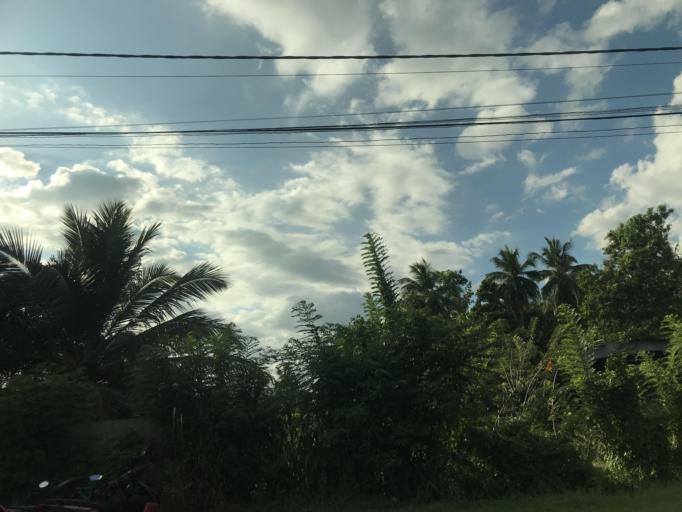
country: LK
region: Western
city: Gampaha
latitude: 7.0624
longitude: 80.0105
